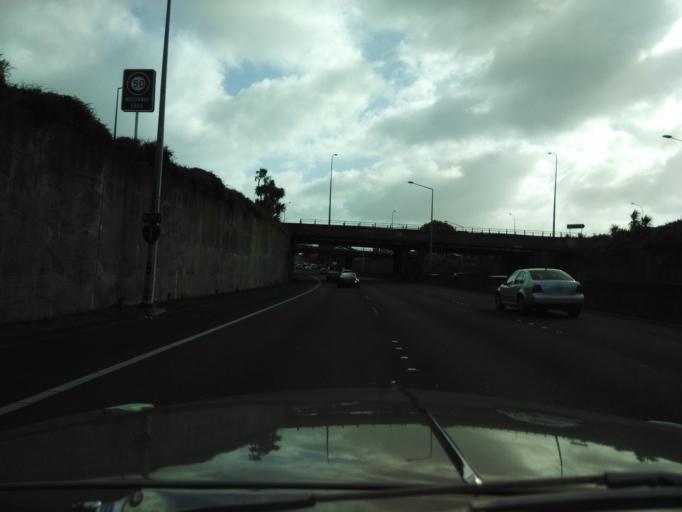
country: NZ
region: Auckland
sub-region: Auckland
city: Auckland
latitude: -36.8898
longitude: 174.7983
